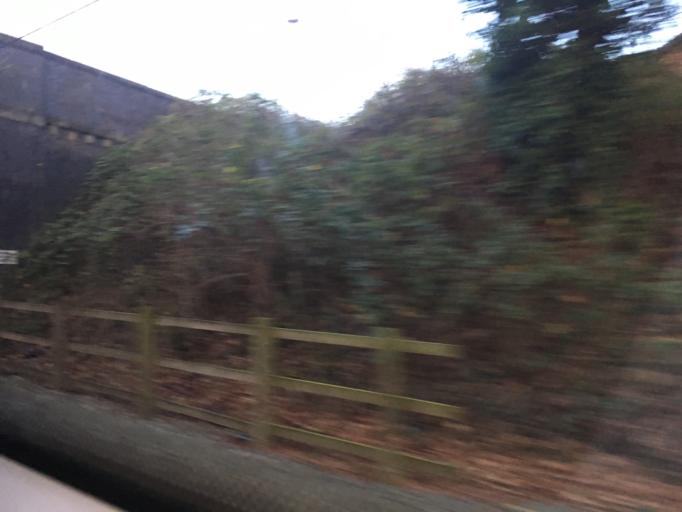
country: GB
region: England
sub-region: Manchester
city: Didsbury
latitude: 53.4205
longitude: -2.2331
